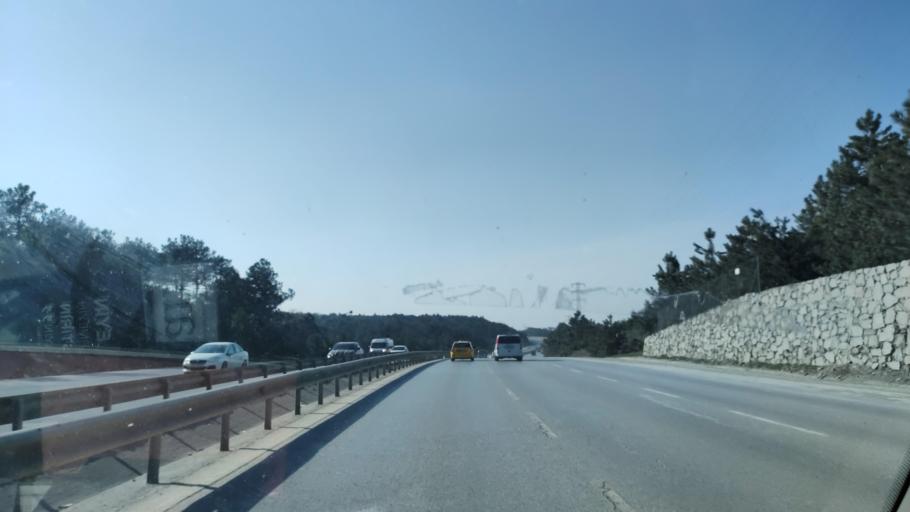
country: TR
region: Istanbul
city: Basaksehir
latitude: 41.1629
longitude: 28.7717
